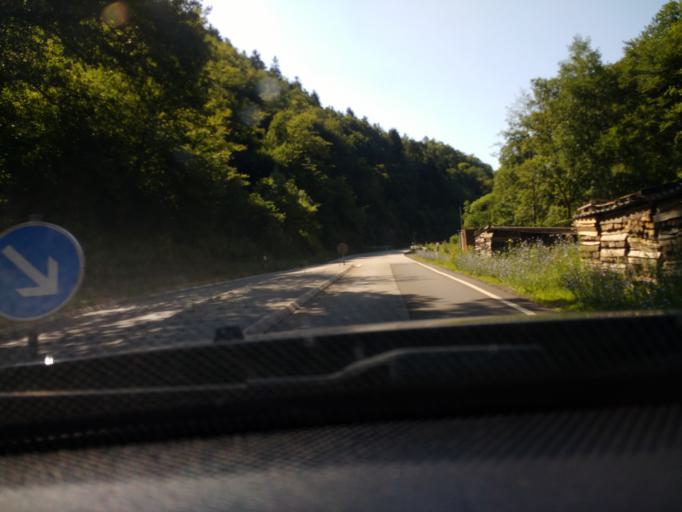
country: DE
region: Rheinland-Pfalz
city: Alf
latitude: 50.0499
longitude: 7.1051
